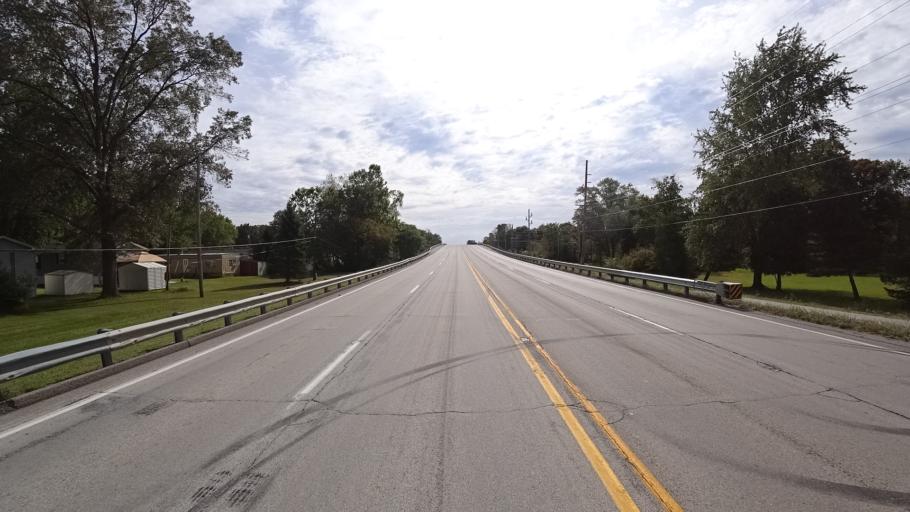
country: US
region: Indiana
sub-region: LaPorte County
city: Trail Creek
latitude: 41.7167
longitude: -86.8260
